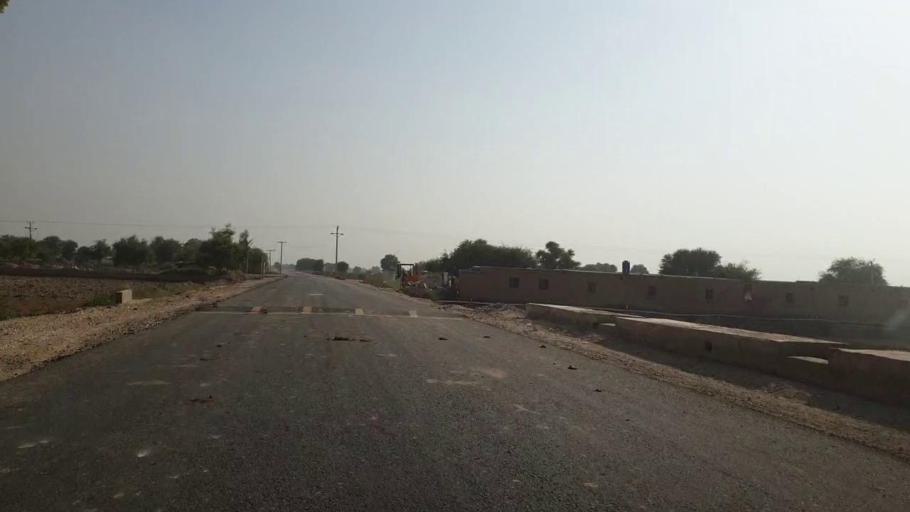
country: PK
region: Sindh
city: Bhan
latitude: 26.5348
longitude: 67.7884
